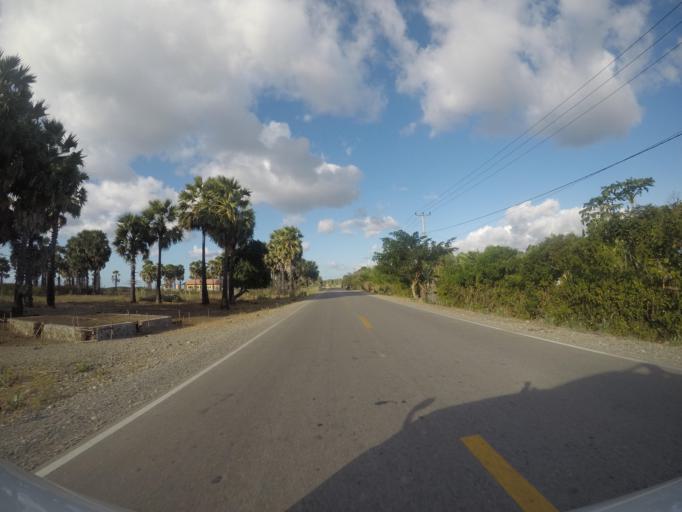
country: TL
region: Lautem
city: Lospalos
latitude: -8.3787
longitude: 126.8668
